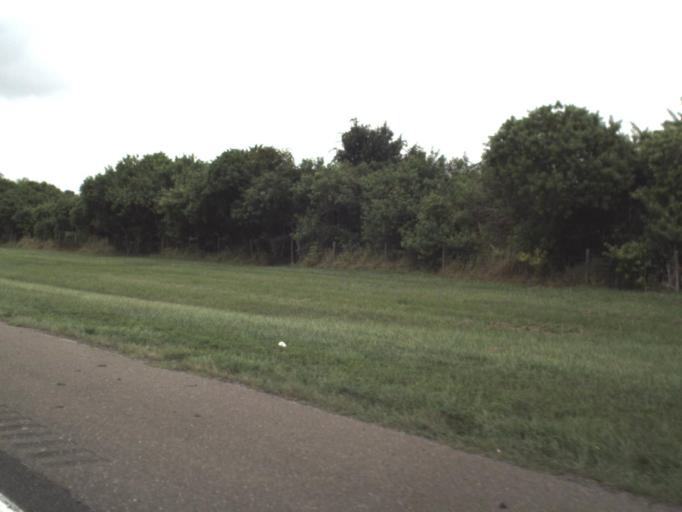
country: US
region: Florida
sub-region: Manatee County
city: Ellenton
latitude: 27.6173
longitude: -82.4847
